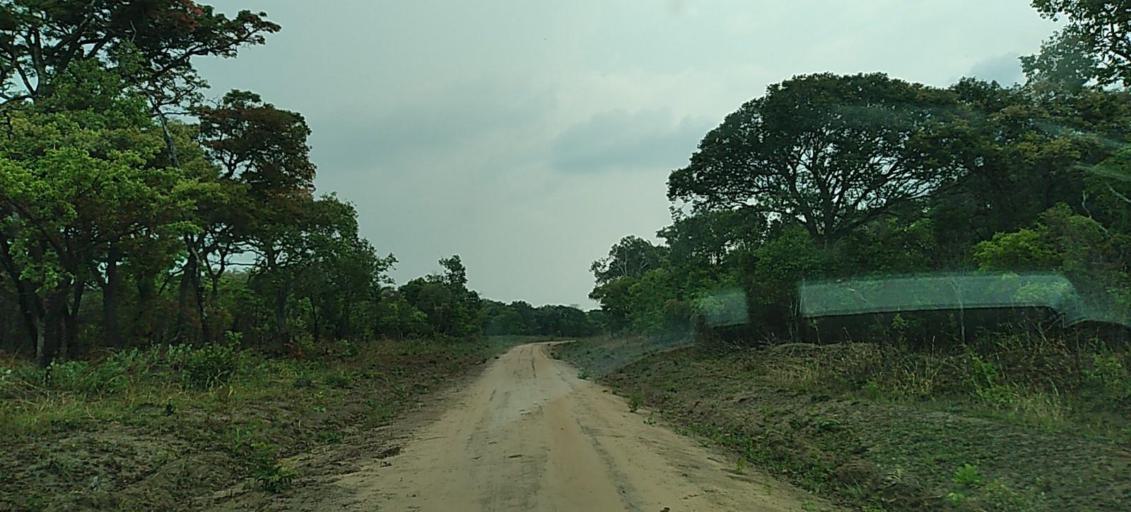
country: ZM
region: North-Western
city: Mwinilunga
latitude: -11.4096
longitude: 24.6195
